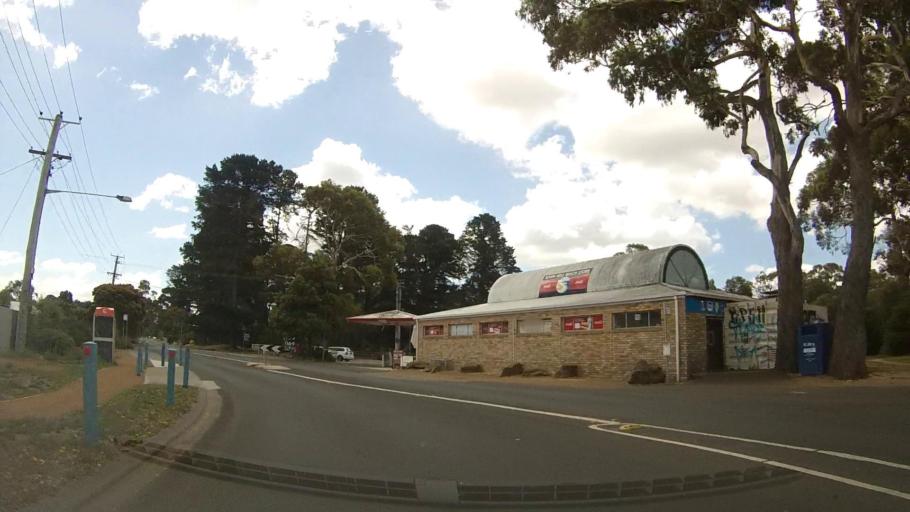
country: AU
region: Tasmania
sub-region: Clarence
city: Seven Mile Beach
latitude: -42.8617
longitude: 147.5055
